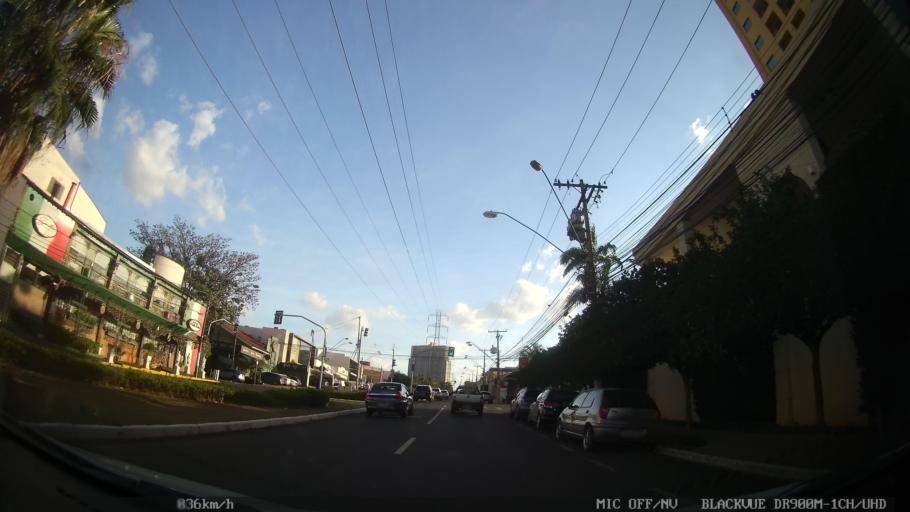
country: BR
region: Sao Paulo
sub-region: Ribeirao Preto
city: Ribeirao Preto
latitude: -21.1939
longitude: -47.8019
